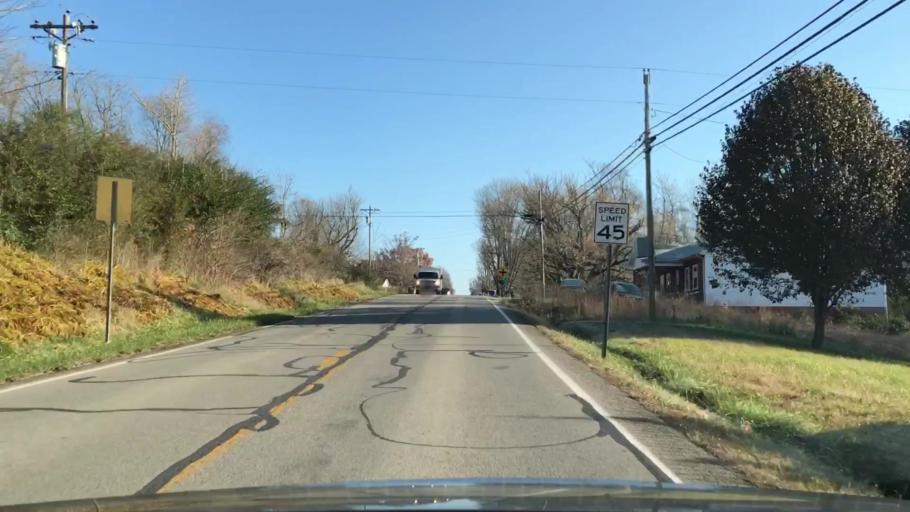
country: US
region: Kentucky
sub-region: Edmonson County
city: Brownsville
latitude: 37.2378
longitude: -86.2917
